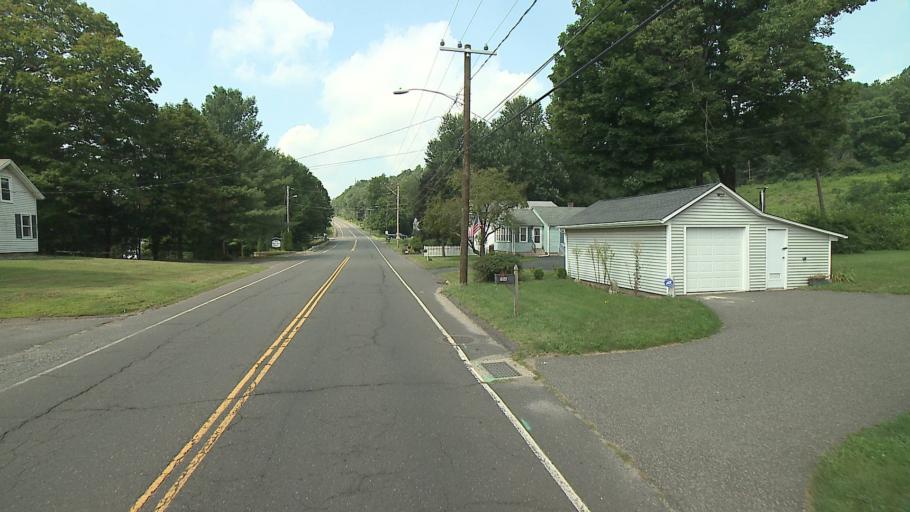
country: US
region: Connecticut
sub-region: Litchfield County
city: Thomaston
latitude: 41.6583
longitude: -73.0956
